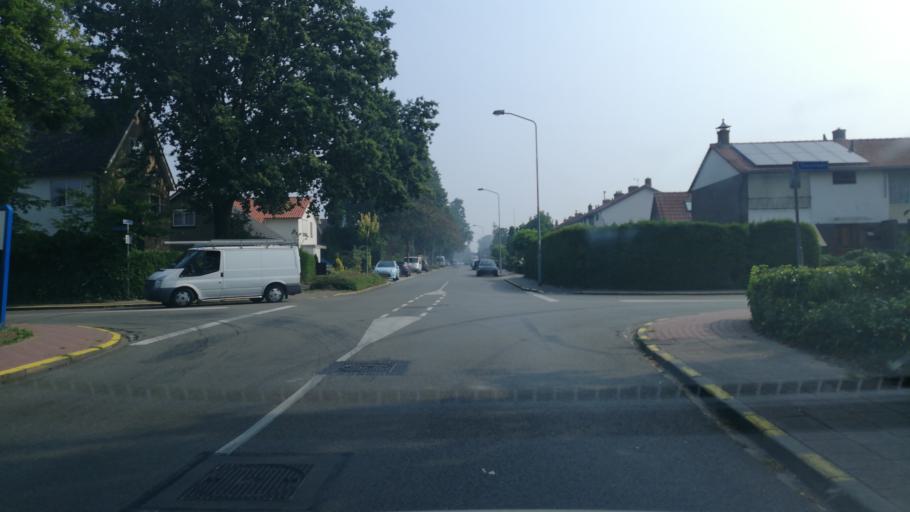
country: NL
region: Gelderland
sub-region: Gemeente Ermelo
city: Ermelo
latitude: 52.2936
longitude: 5.6109
